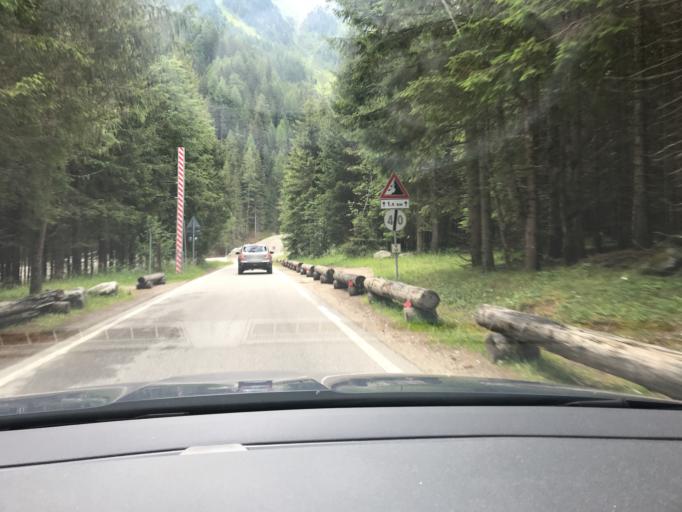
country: IT
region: Trentino-Alto Adige
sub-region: Bolzano
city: San Martino
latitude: 46.8825
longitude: 12.1641
